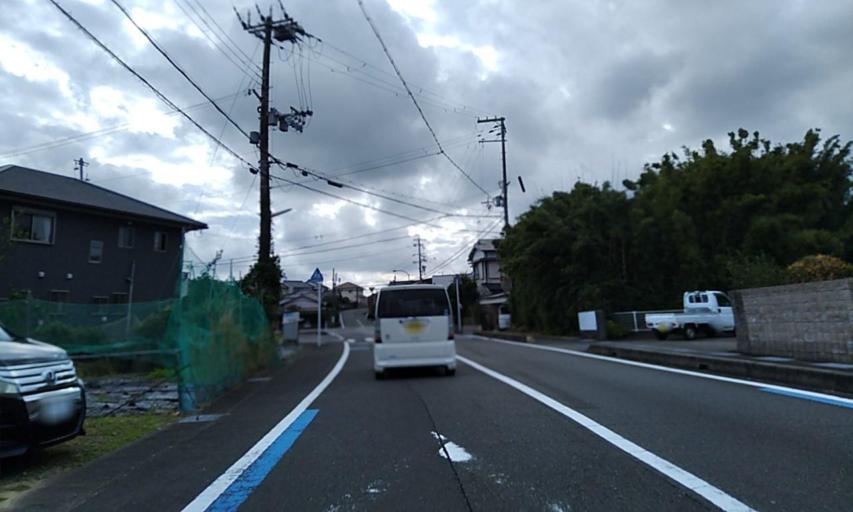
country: JP
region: Wakayama
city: Shingu
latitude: 33.5870
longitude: 135.9483
